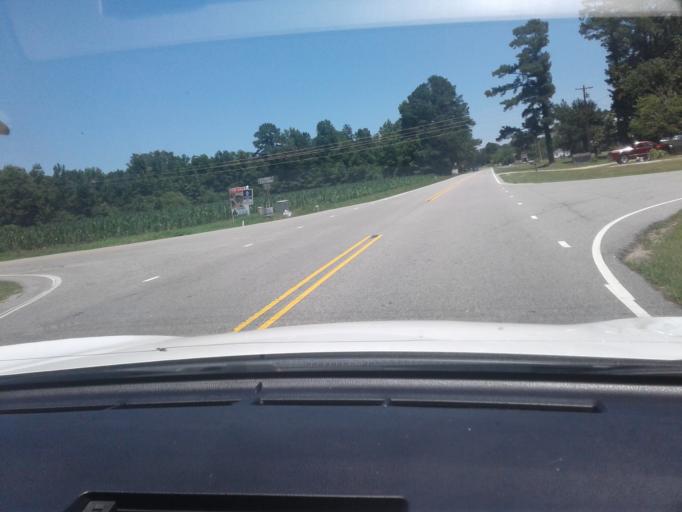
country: US
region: North Carolina
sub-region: Harnett County
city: Lillington
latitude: 35.3673
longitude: -78.8882
